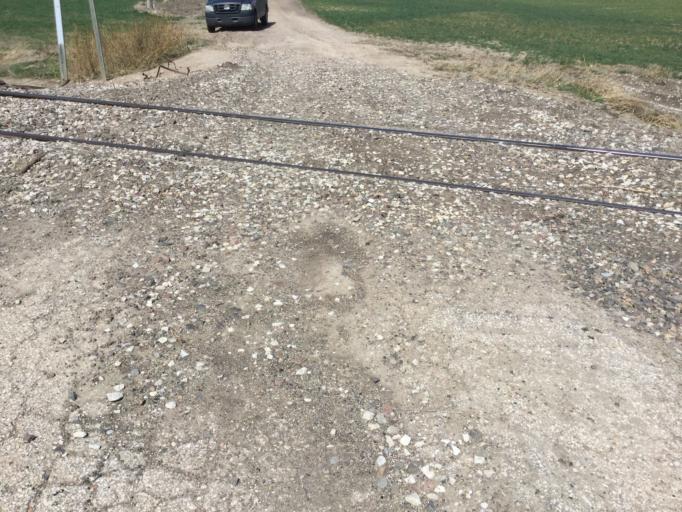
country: US
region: Kansas
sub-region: Barton County
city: Great Bend
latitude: 38.4278
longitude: -98.9039
